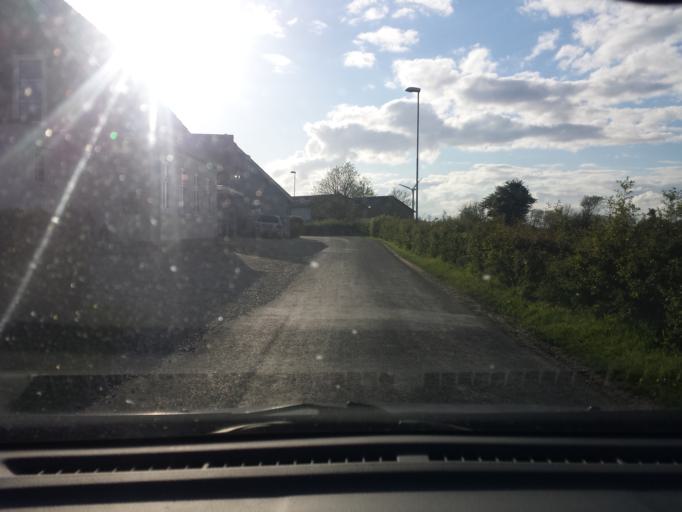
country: DK
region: South Denmark
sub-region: Langeland Kommune
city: Rudkobing
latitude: 54.9136
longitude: 10.7577
